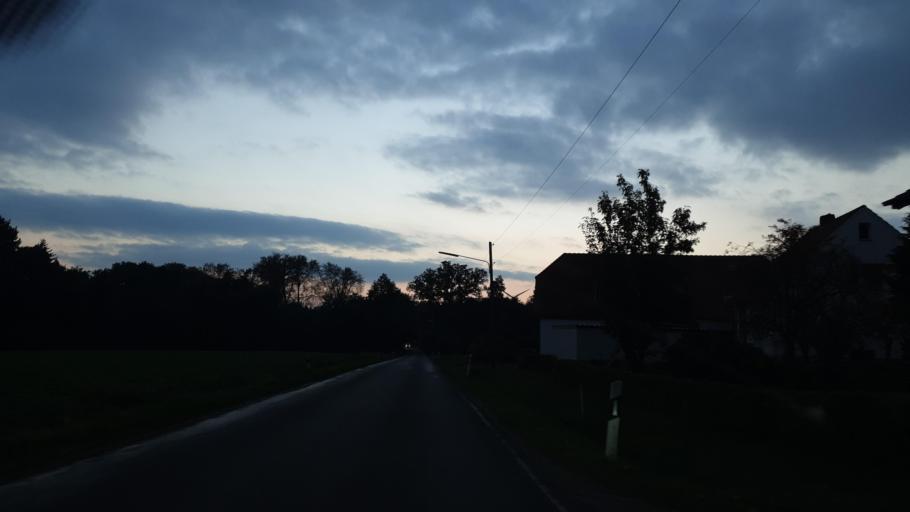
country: DE
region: North Rhine-Westphalia
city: Loehne
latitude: 52.2426
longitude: 8.7139
